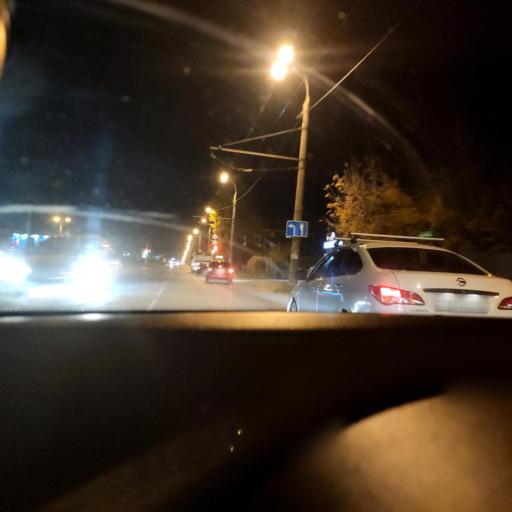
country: RU
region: Samara
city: Petra-Dubrava
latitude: 53.2553
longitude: 50.2659
